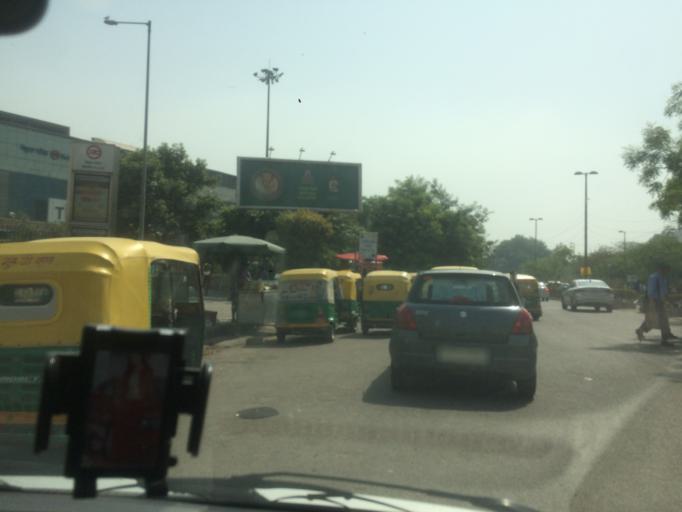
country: IN
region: Uttar Pradesh
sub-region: Gautam Buddha Nagar
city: Noida
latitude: 28.5505
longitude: 77.2512
